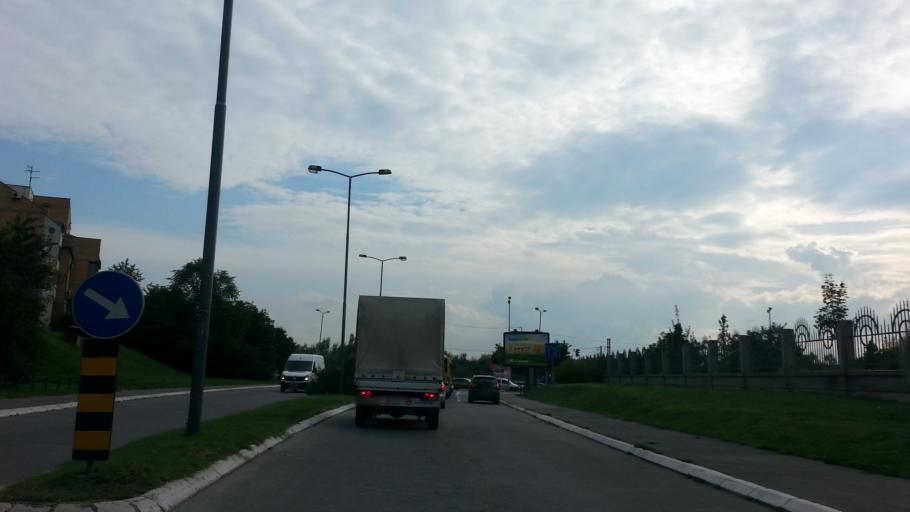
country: RS
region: Central Serbia
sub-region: Belgrade
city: Cukarica
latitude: 44.7756
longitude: 20.4076
